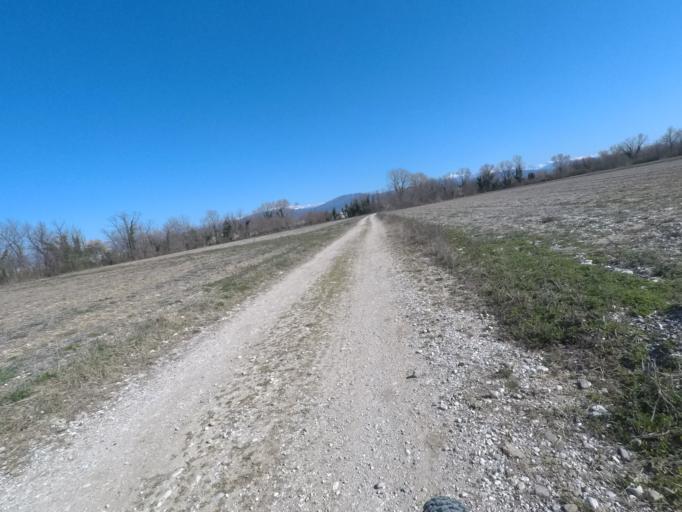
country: IT
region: Friuli Venezia Giulia
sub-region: Provincia di Udine
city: Remanzacco
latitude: 46.0657
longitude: 13.3293
